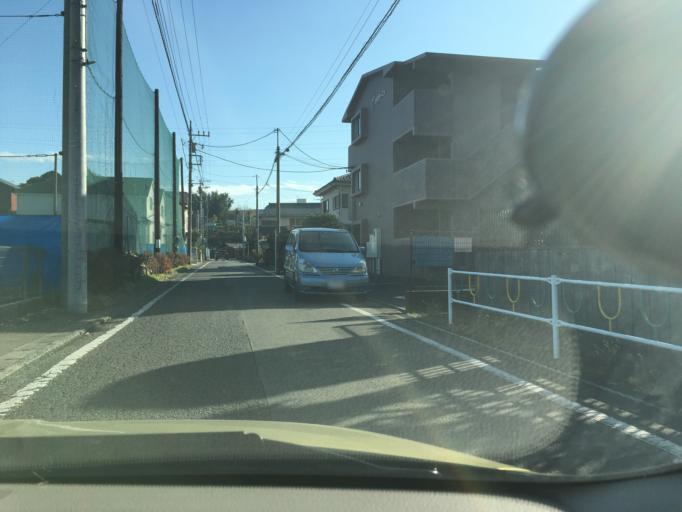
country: JP
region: Tokyo
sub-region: Machida-shi
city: Machida
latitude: 35.5630
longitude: 139.4147
